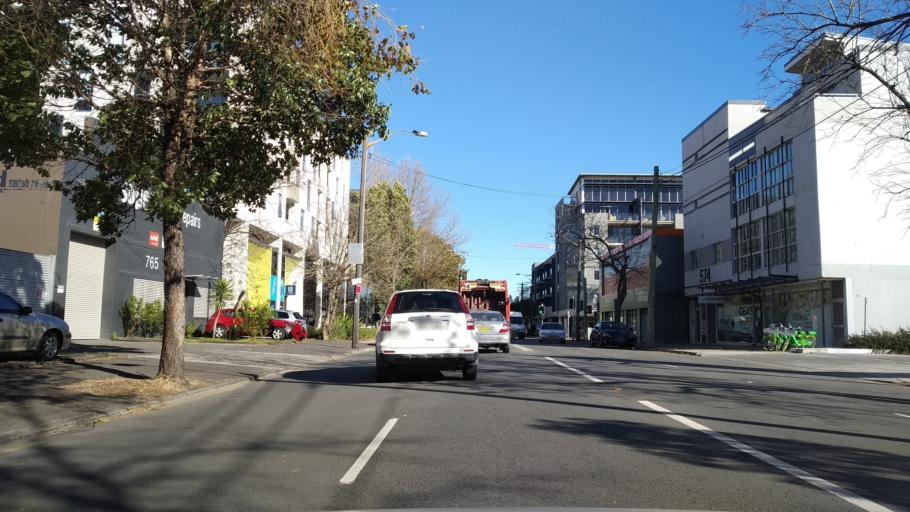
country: AU
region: New South Wales
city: Alexandria
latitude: -33.9177
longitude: 151.1995
